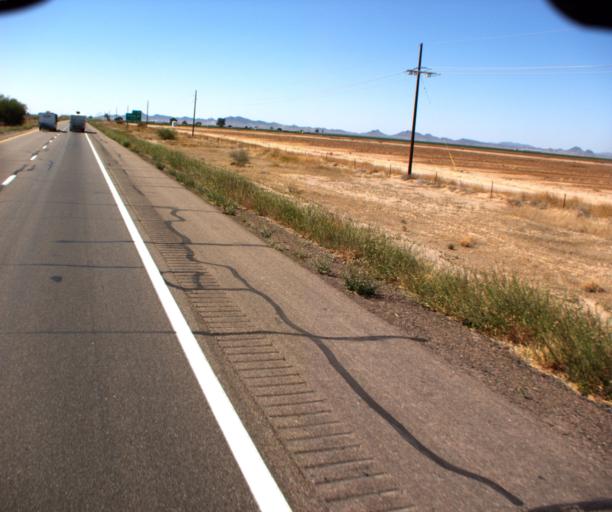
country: US
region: Arizona
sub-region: Maricopa County
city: Gila Bend
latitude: 32.9239
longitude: -112.8735
